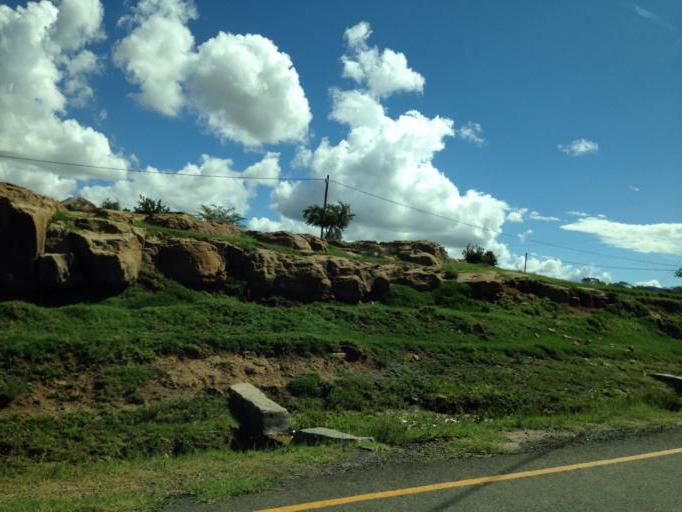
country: LS
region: Mafeteng
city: Mafeteng
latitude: -29.6937
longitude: 27.4418
